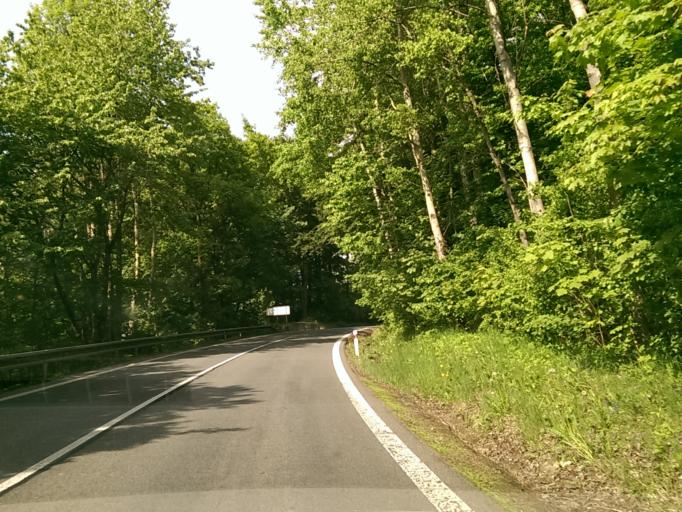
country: CZ
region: Liberecky
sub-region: Okres Semily
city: Turnov
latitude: 50.6156
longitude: 15.1653
